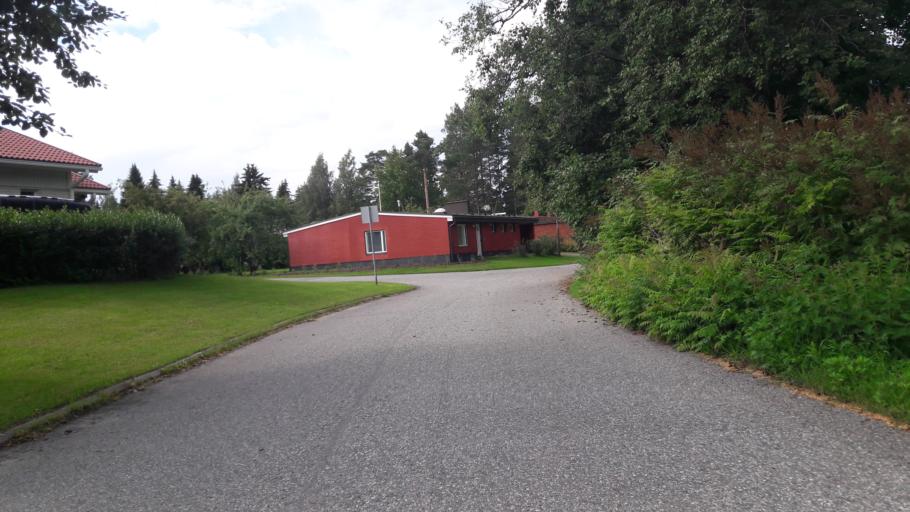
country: FI
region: North Karelia
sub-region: Joensuu
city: Joensuu
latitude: 62.5845
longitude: 29.8063
